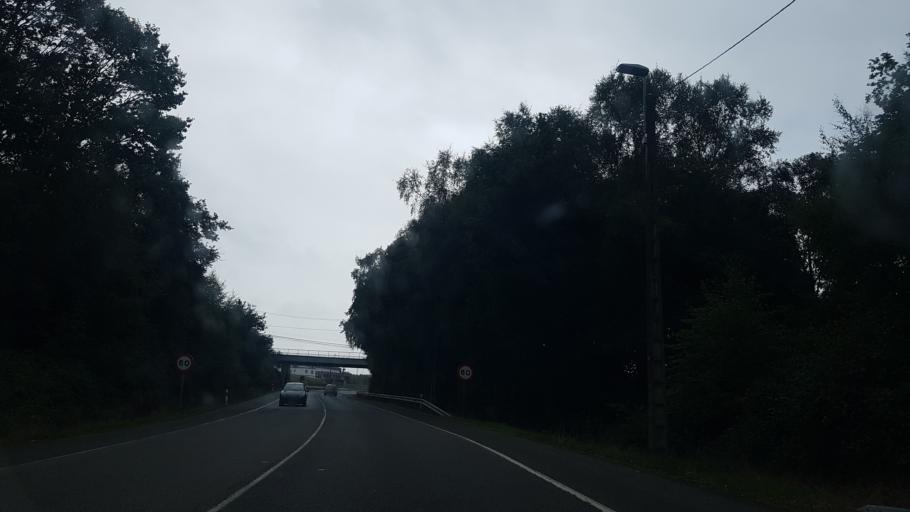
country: ES
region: Galicia
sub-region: Provincia de Lugo
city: Lugo
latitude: 42.9887
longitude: -7.5897
